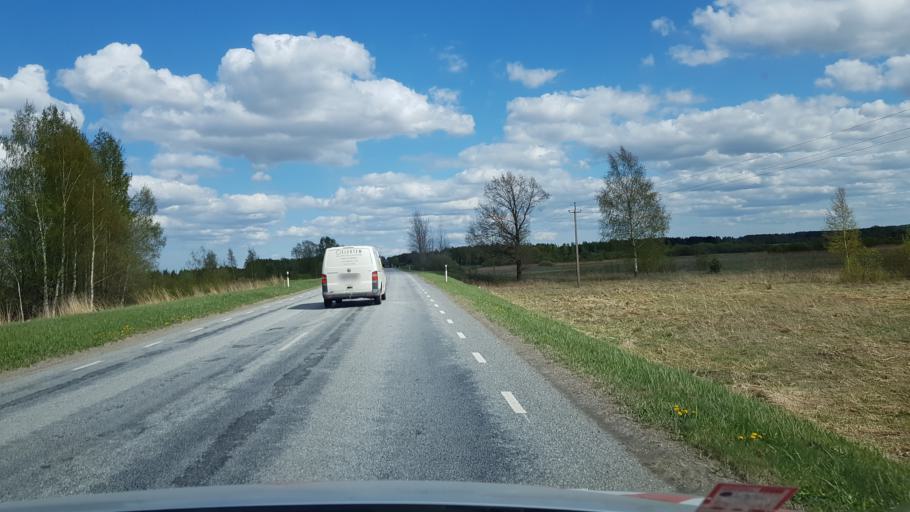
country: EE
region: Tartu
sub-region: UElenurme vald
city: Ulenurme
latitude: 58.3278
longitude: 26.7537
